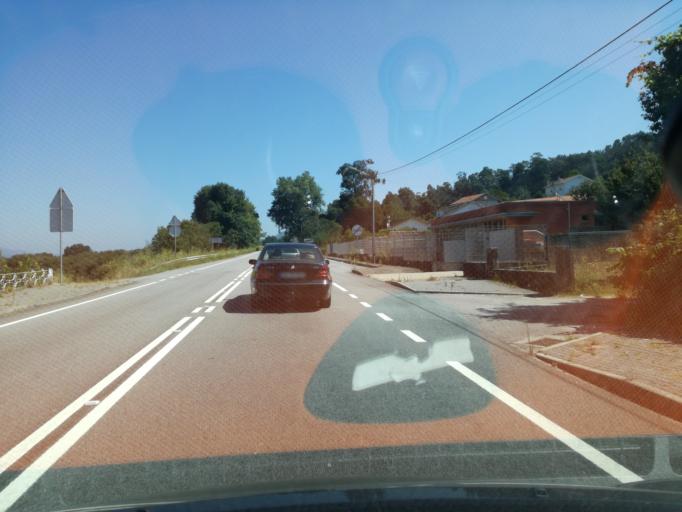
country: ES
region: Galicia
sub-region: Provincia de Pontevedra
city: O Rosal
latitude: 41.9115
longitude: -8.7885
